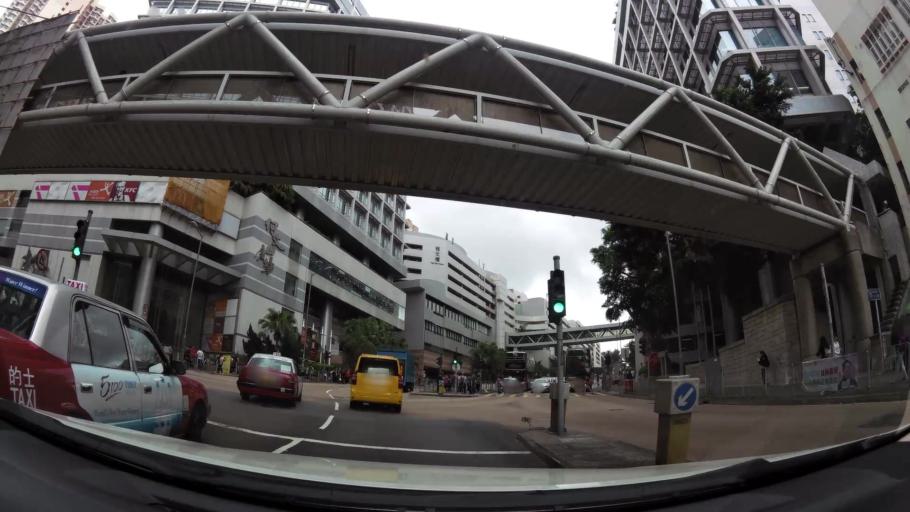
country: HK
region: Kowloon City
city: Kowloon
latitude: 22.3163
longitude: 114.1810
